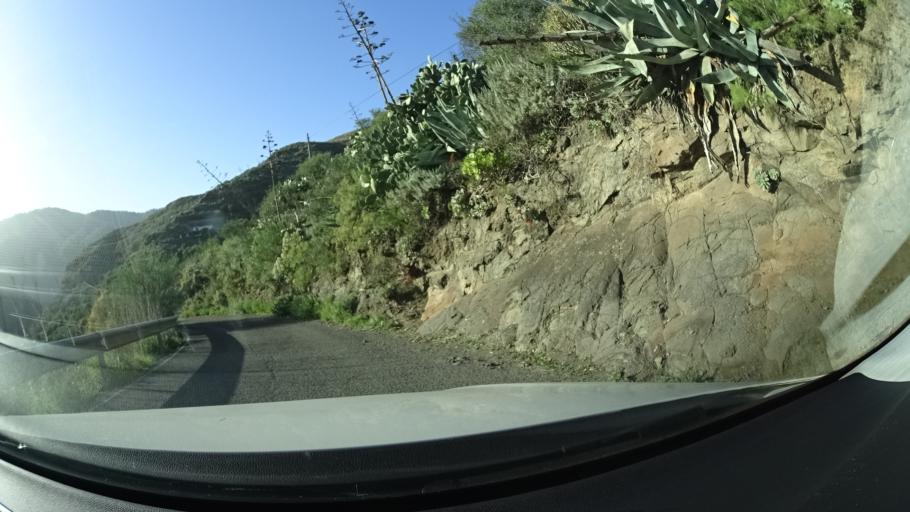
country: ES
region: Canary Islands
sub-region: Provincia de Las Palmas
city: Artenara
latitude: 28.0450
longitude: -15.6569
